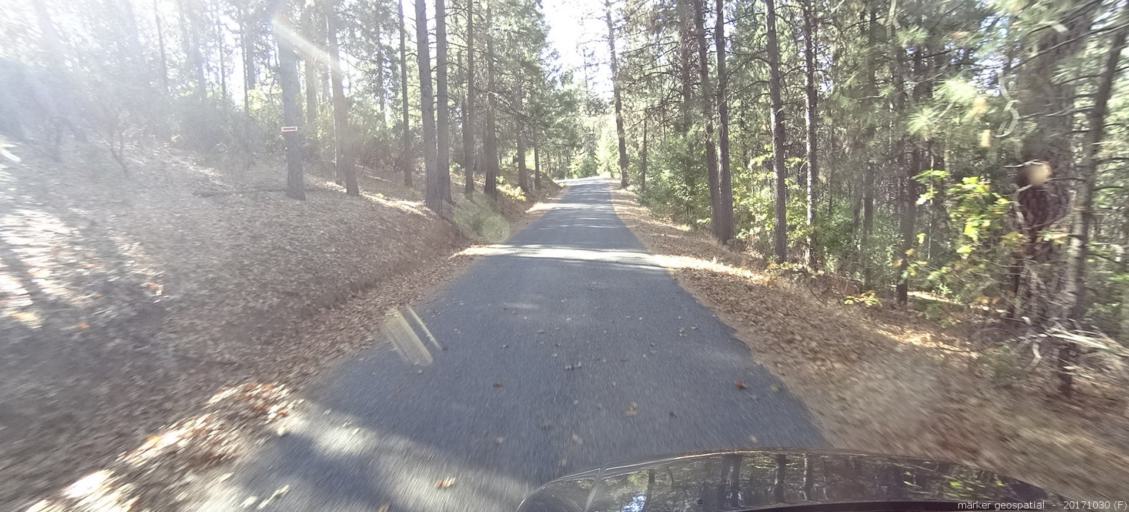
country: US
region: California
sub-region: Shasta County
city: Shingletown
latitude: 40.5873
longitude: -121.8631
